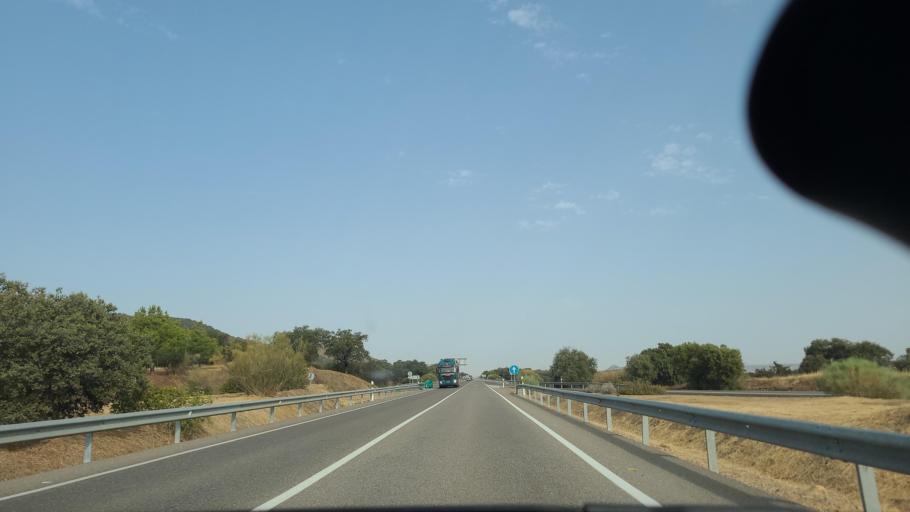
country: ES
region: Andalusia
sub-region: Province of Cordoba
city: Belmez
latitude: 38.2143
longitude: -5.1417
